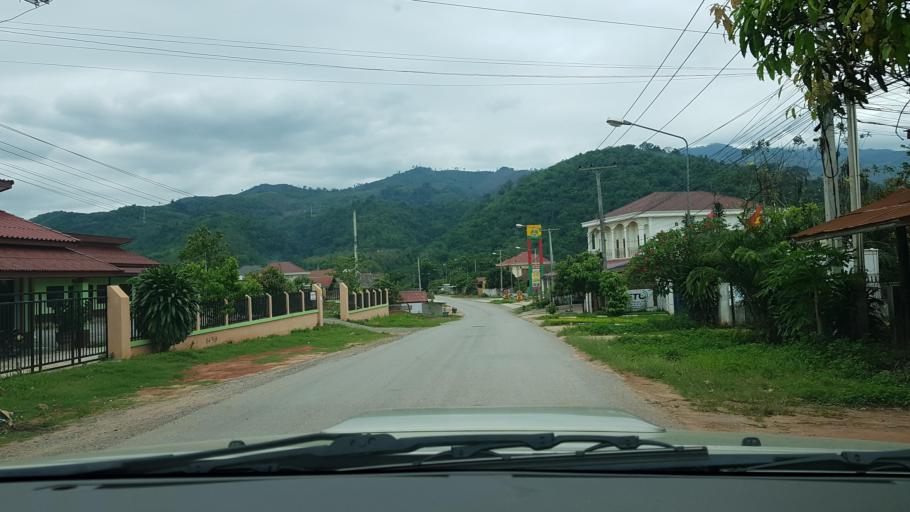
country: LA
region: Oudomxai
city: Muang Xay
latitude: 20.6988
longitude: 101.9997
